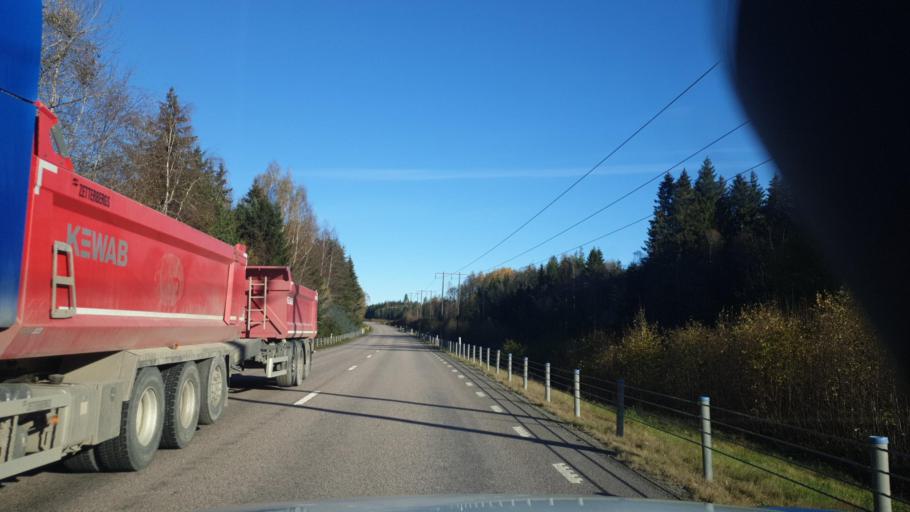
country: SE
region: Vaermland
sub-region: Karlstads Kommun
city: Edsvalla
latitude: 59.4260
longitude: 13.1951
